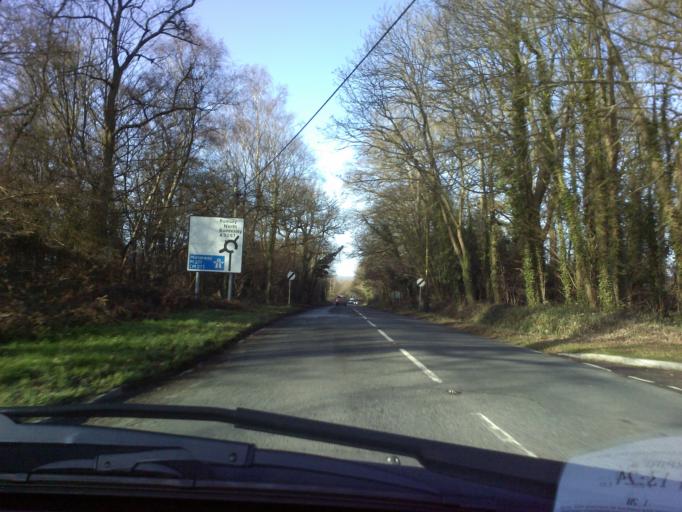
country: GB
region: England
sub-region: Hampshire
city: Totton
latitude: 50.9528
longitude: -1.4694
